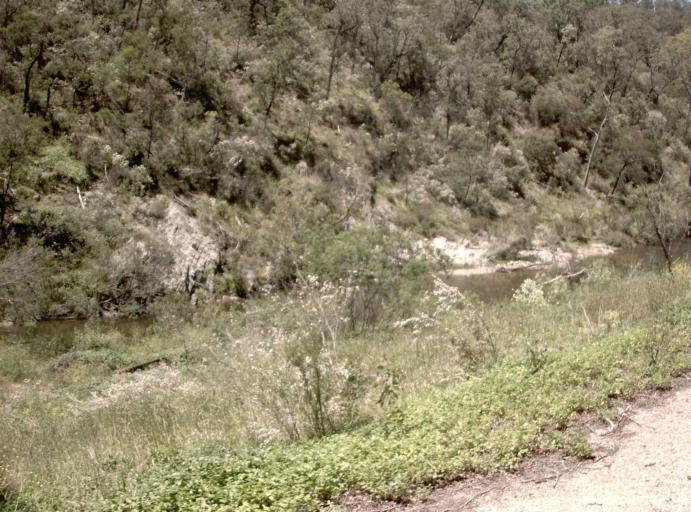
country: AU
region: Victoria
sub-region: East Gippsland
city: Bairnsdale
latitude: -37.4637
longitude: 147.8319
